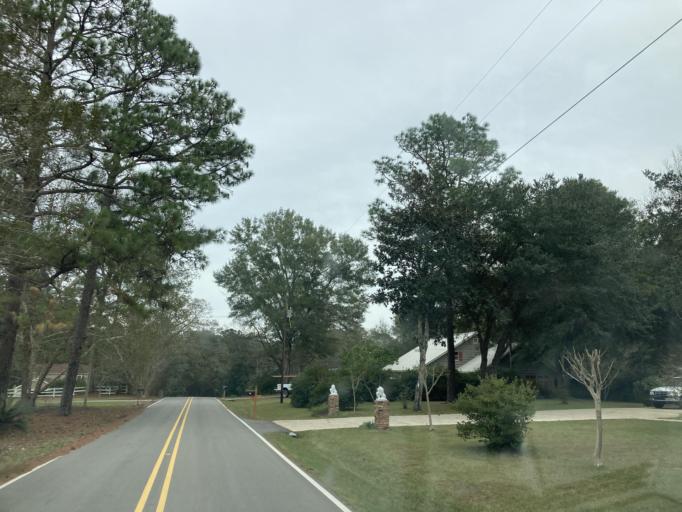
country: US
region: Mississippi
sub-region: Lamar County
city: Purvis
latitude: 31.1104
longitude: -89.4148
